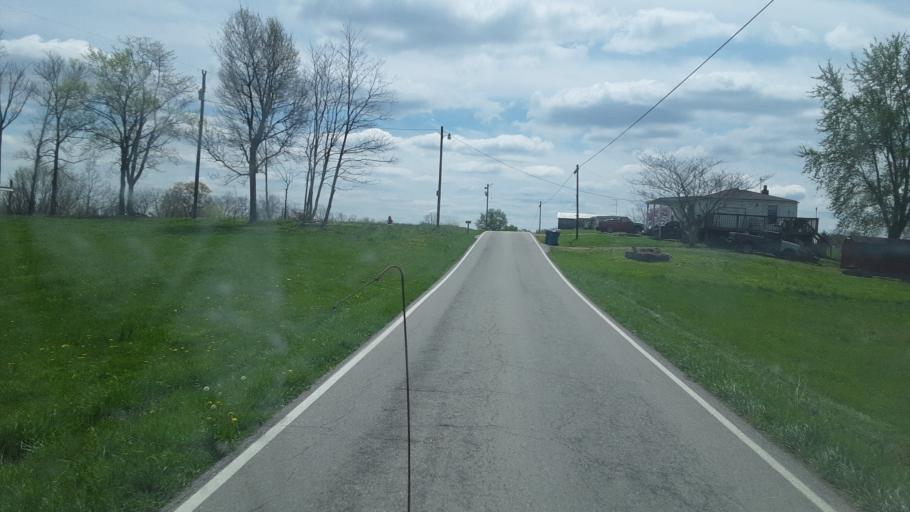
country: US
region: Kentucky
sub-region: Owen County
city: Owenton
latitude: 38.6578
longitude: -84.7721
